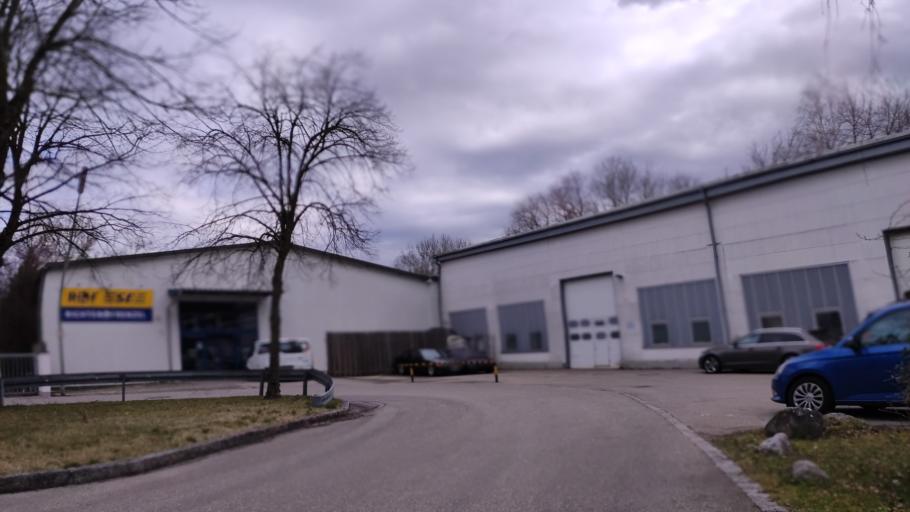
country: DE
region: Bavaria
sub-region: Upper Bavaria
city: Emmering
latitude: 48.1828
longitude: 11.2917
